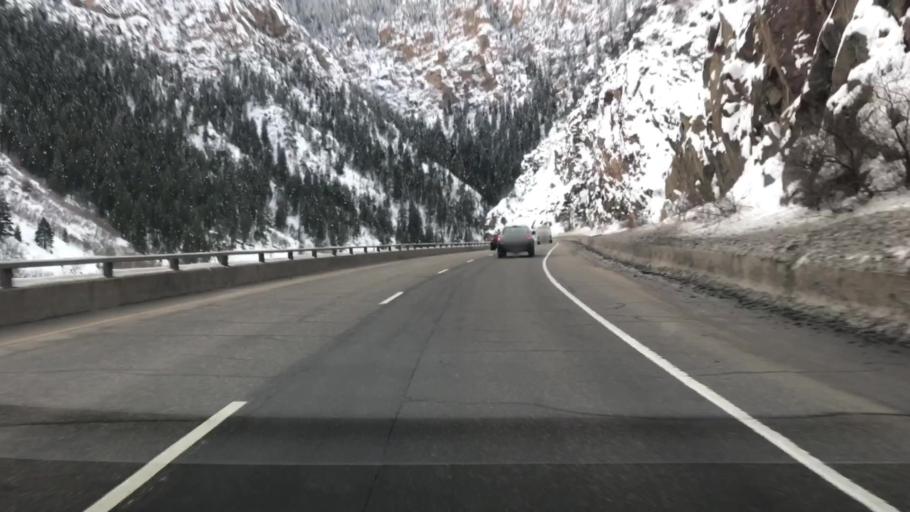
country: US
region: Colorado
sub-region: Garfield County
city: Glenwood Springs
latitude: 39.5604
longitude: -107.2404
